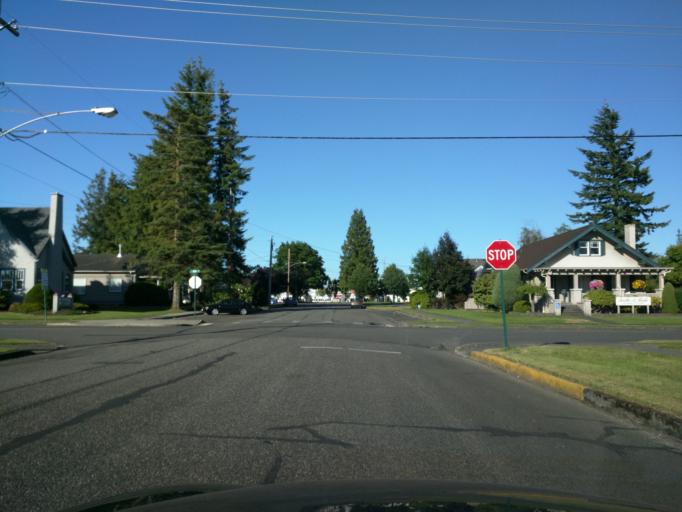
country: US
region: Washington
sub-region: Whatcom County
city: Lynden
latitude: 48.9455
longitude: -122.4554
